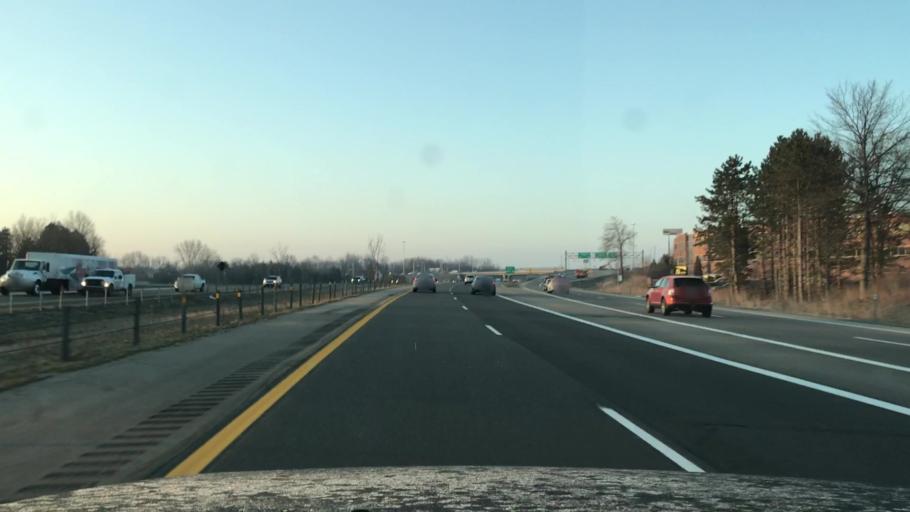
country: US
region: Michigan
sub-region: Kent County
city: East Grand Rapids
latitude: 42.9517
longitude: -85.5680
